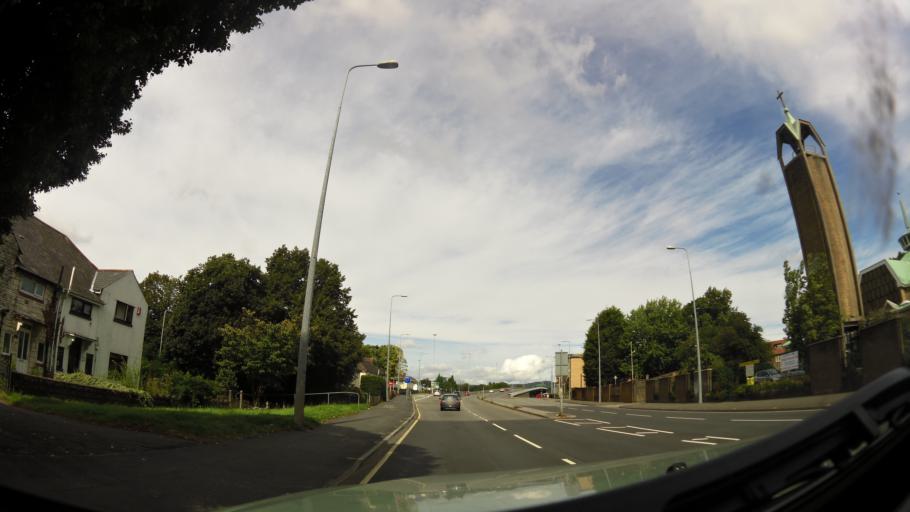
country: GB
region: Wales
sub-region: Cardiff
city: Cardiff
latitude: 51.5016
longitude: -3.1964
